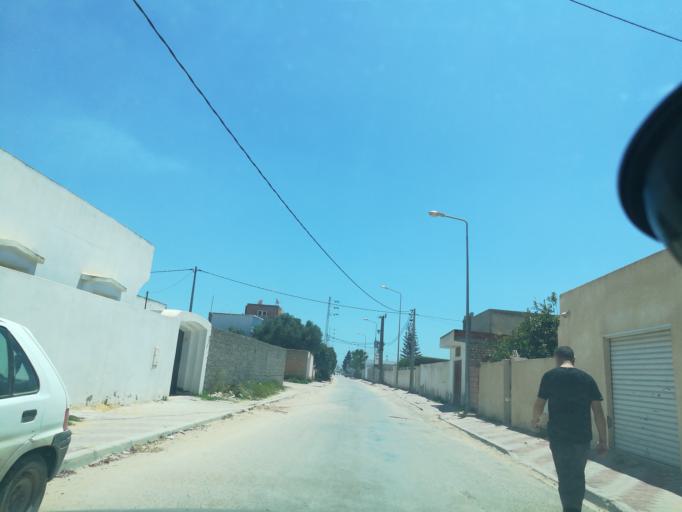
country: TN
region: Safaqis
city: Al Qarmadah
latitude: 34.8226
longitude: 10.7556
